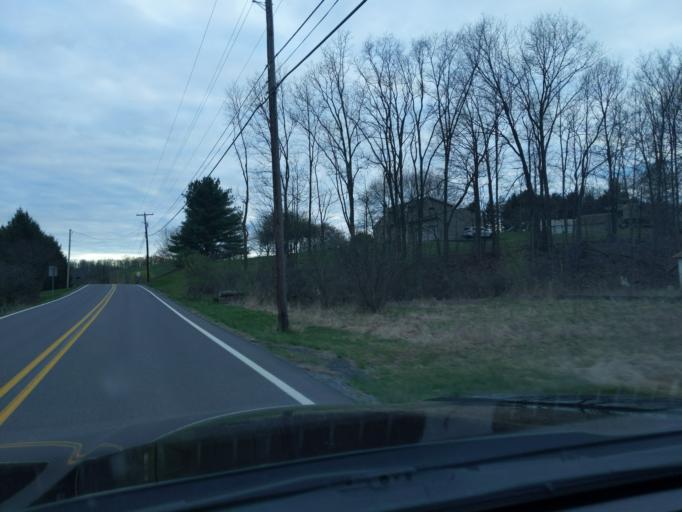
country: US
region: Pennsylvania
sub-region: Blair County
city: Lakemont
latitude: 40.4630
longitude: -78.3461
